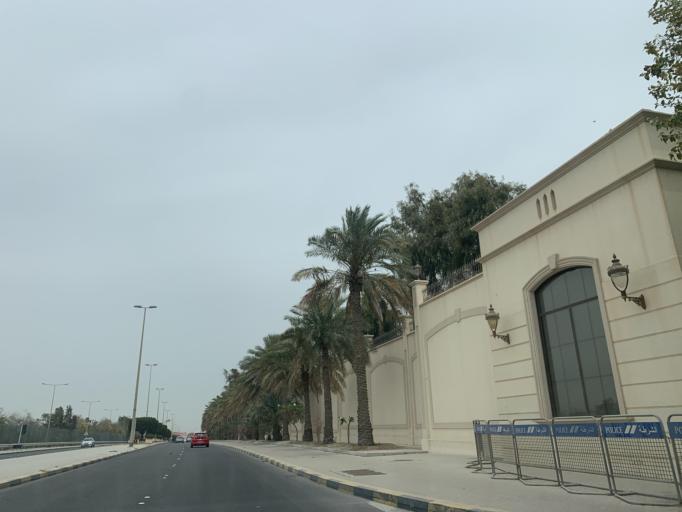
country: BH
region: Northern
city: Ar Rifa'
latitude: 26.1386
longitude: 50.5432
